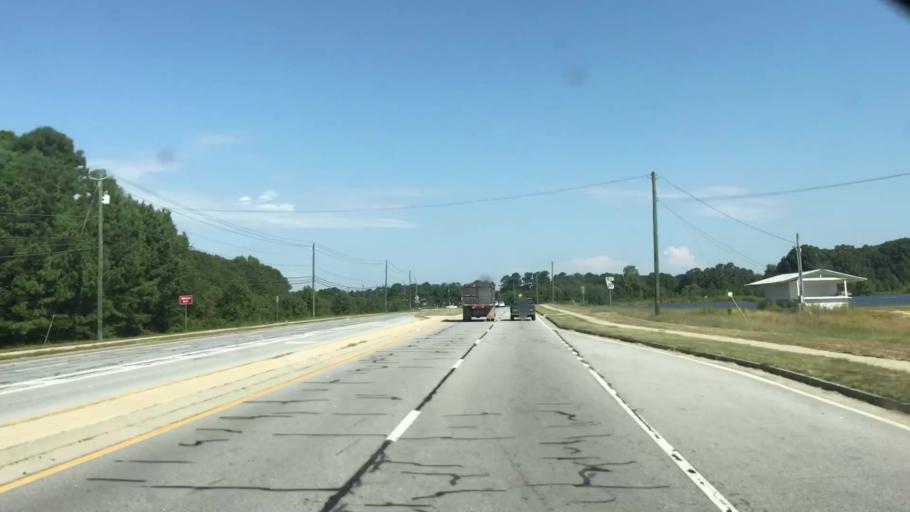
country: US
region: Georgia
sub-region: Walton County
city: Loganville
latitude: 33.8634
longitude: -83.9085
